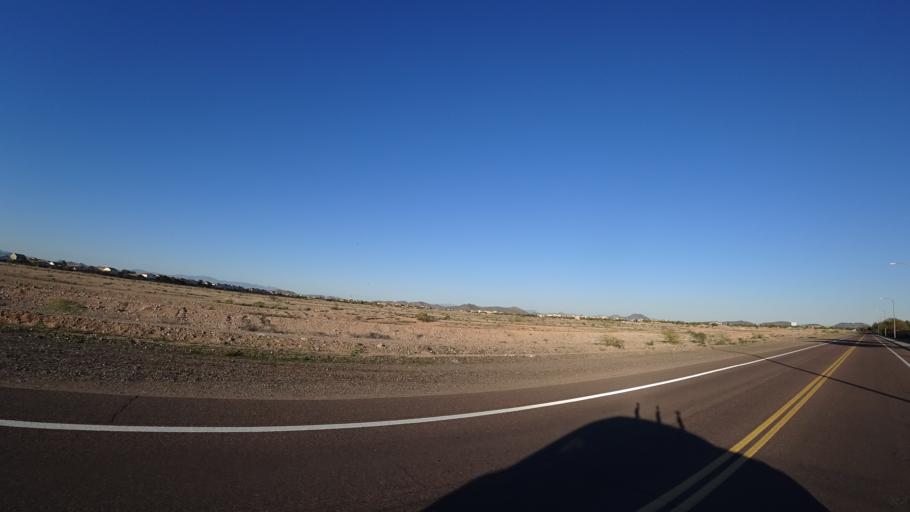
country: US
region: Arizona
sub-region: Maricopa County
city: Sun City West
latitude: 33.6744
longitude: -112.2857
